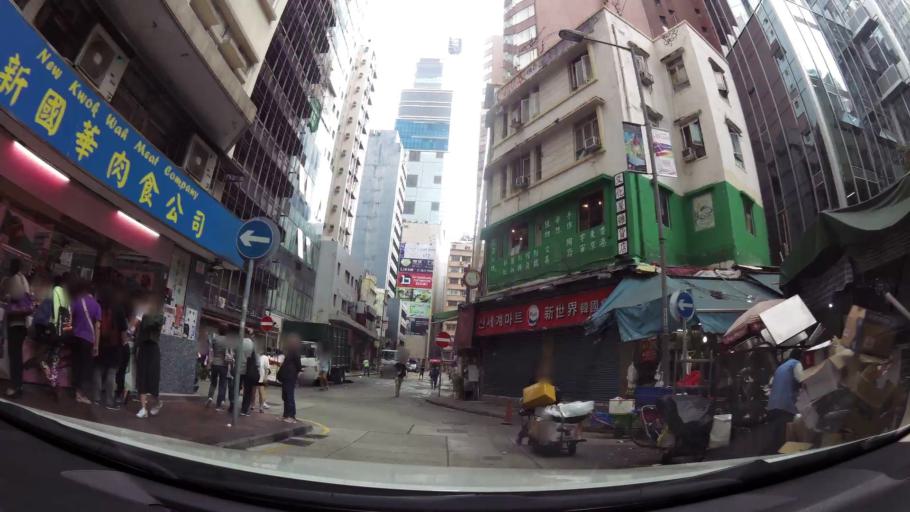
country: HK
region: Kowloon City
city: Kowloon
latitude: 22.3005
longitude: 114.1746
